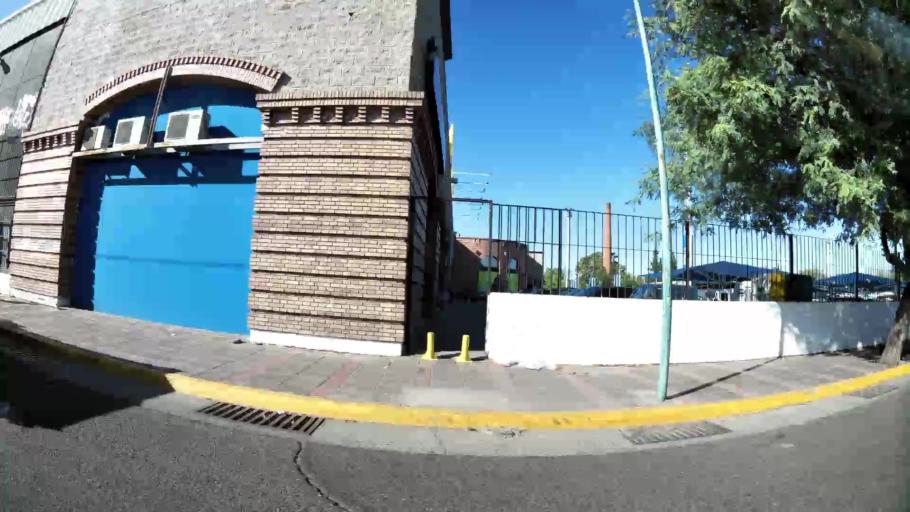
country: AR
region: Mendoza
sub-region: Departamento de Godoy Cruz
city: Godoy Cruz
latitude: -32.9225
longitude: -68.8457
